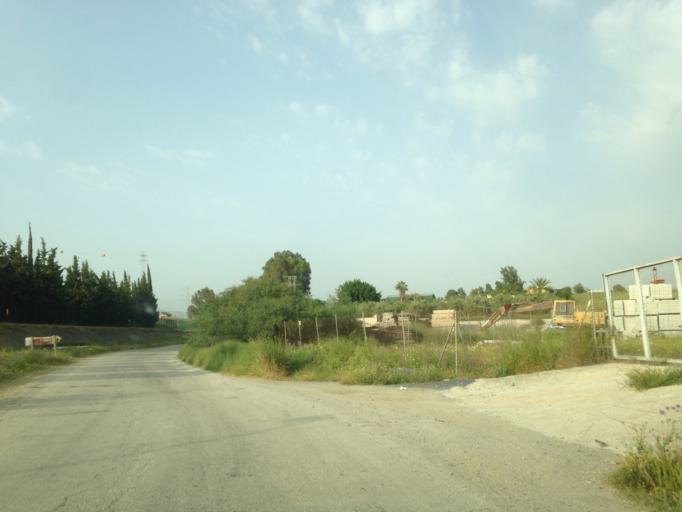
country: ES
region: Andalusia
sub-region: Provincia de Malaga
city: Estacion de Cartama
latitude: 36.7439
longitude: -4.5641
